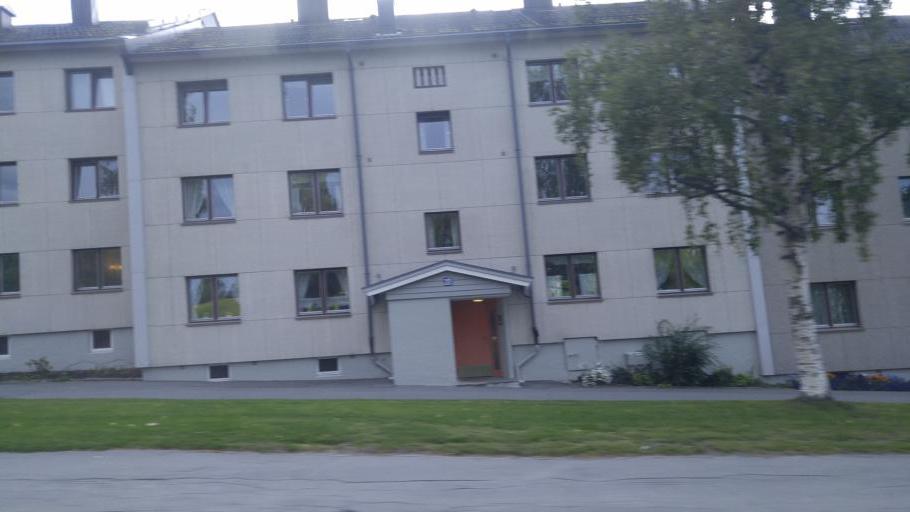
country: NO
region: Sor-Trondelag
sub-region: Trondheim
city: Trondheim
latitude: 63.4150
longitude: 10.3526
